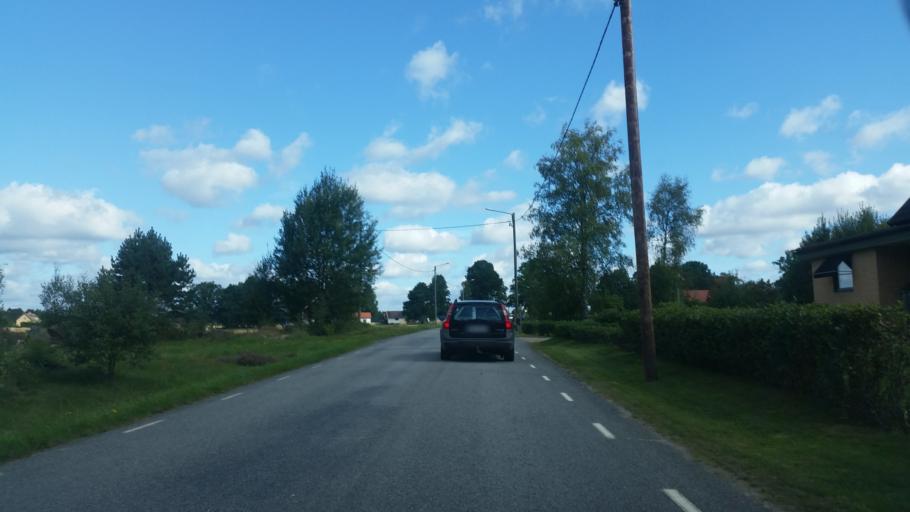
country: SE
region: Joenkoeping
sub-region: Varnamo Kommun
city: Forsheda
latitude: 57.1751
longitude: 13.8423
